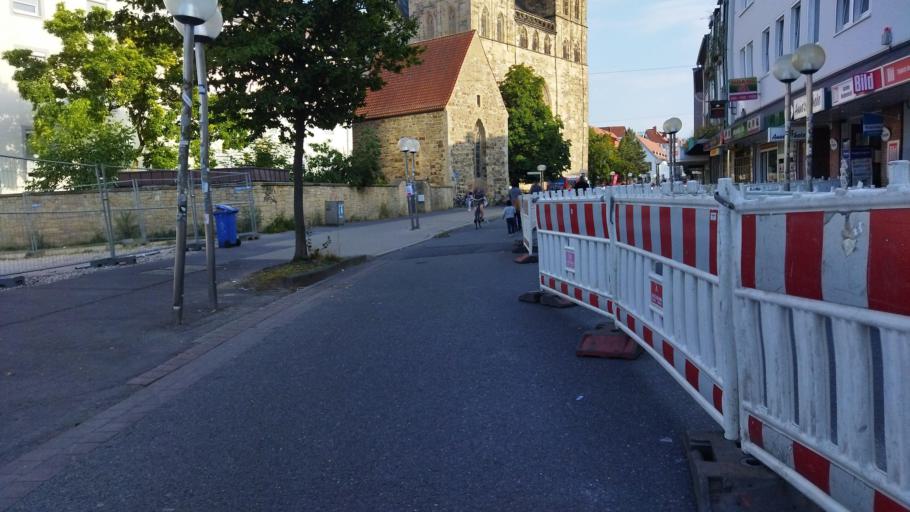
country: DE
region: Lower Saxony
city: Osnabrueck
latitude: 52.2712
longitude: 8.0502
